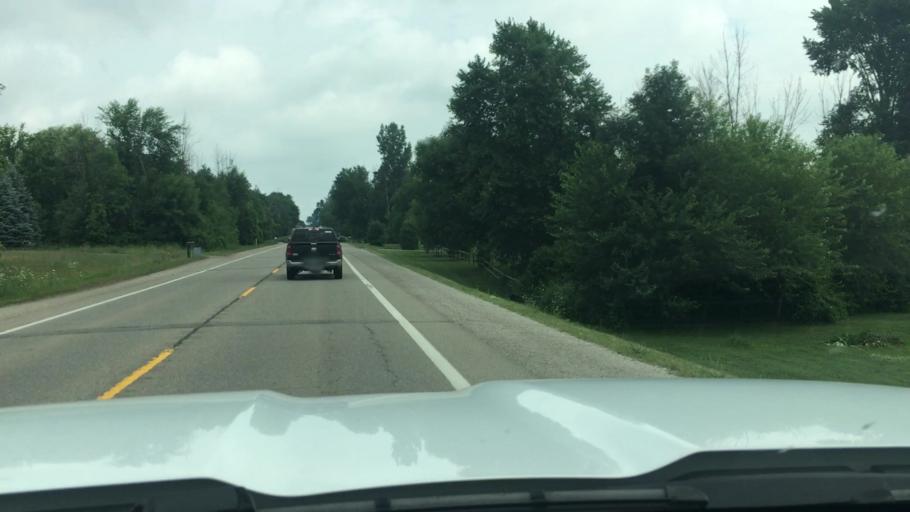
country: US
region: Michigan
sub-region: Lapeer County
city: Imlay City
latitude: 43.0884
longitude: -83.0741
